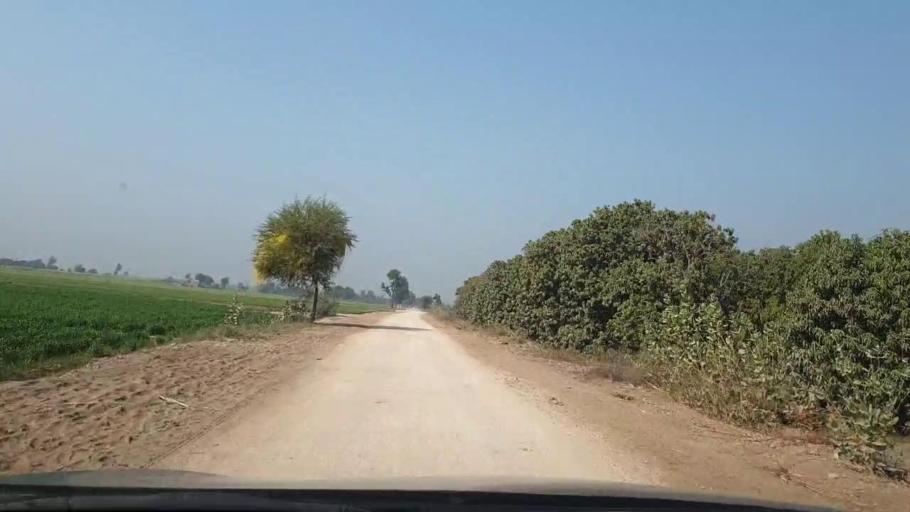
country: PK
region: Sindh
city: Tando Allahyar
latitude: 25.5180
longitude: 68.7479
